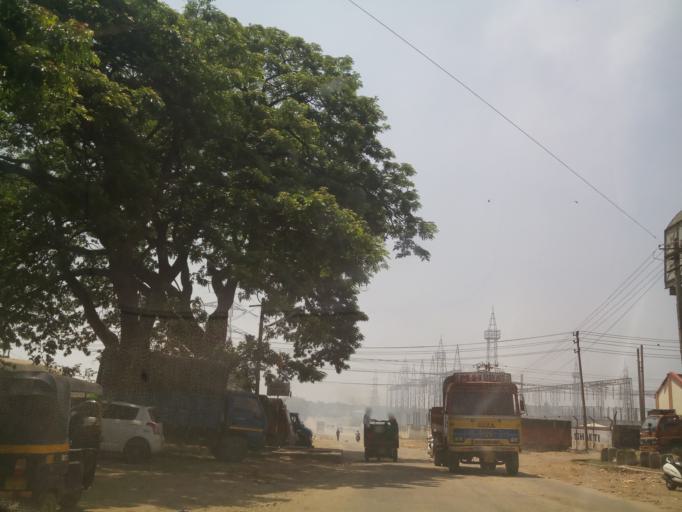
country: IN
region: Karnataka
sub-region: Hassan
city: Hassan
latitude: 12.9986
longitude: 76.0938
